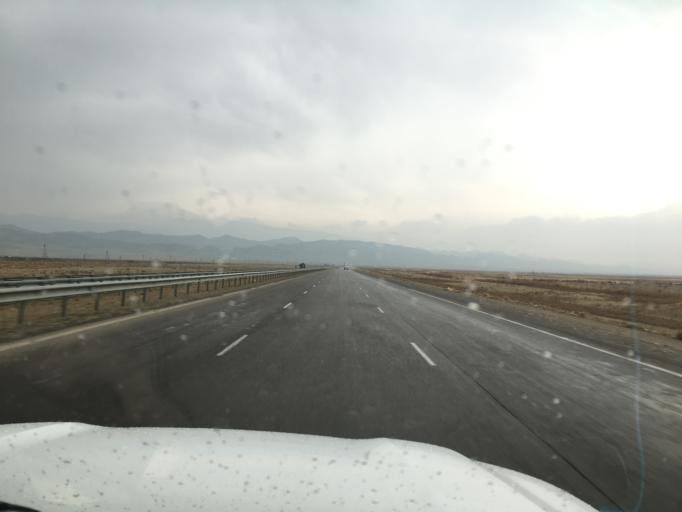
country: IR
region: Razavi Khorasan
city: Dargaz
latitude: 37.5921
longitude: 59.2541
